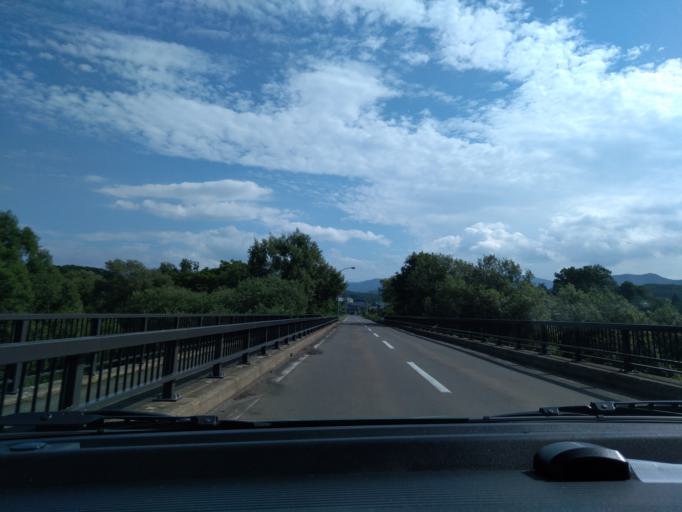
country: JP
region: Iwate
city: Shizukuishi
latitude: 39.6664
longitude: 140.9821
